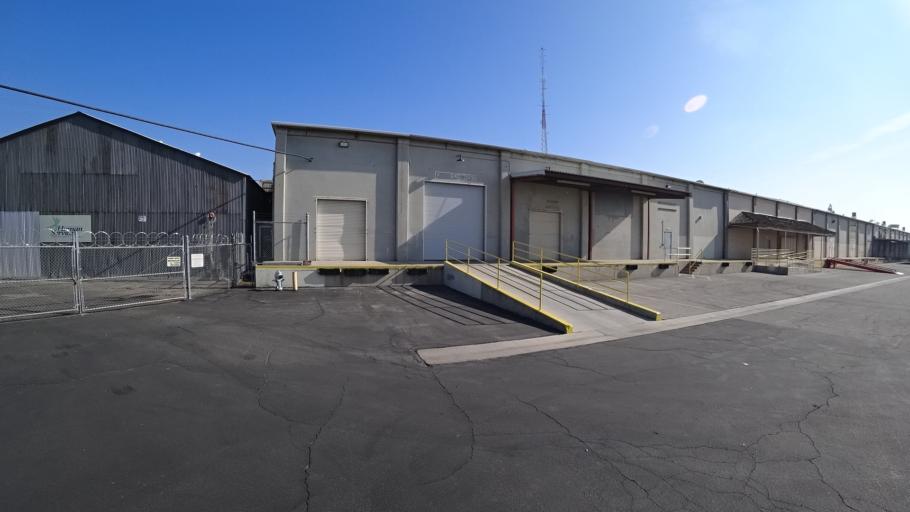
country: US
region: California
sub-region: Kern County
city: Bakersfield
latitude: 35.3704
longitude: -119.0072
